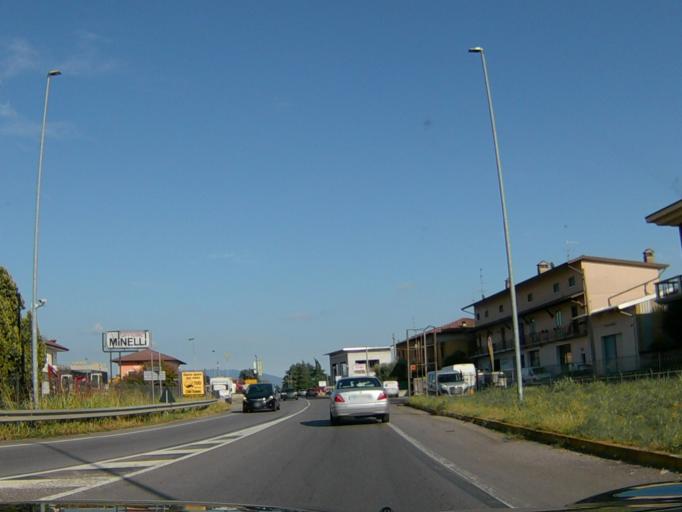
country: IT
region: Lombardy
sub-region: Provincia di Brescia
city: Lodetto
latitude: 45.5581
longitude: 10.0417
